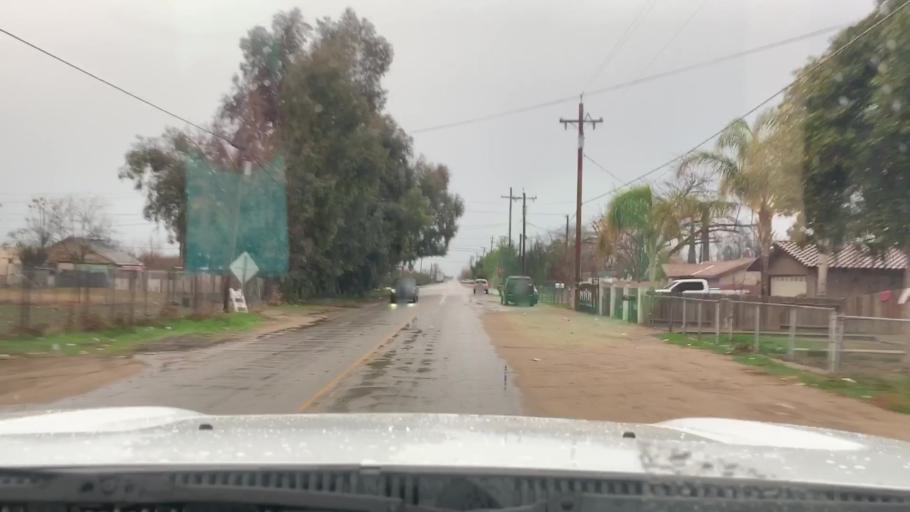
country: US
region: California
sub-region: Kern County
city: Shafter
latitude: 35.4781
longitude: -119.2775
